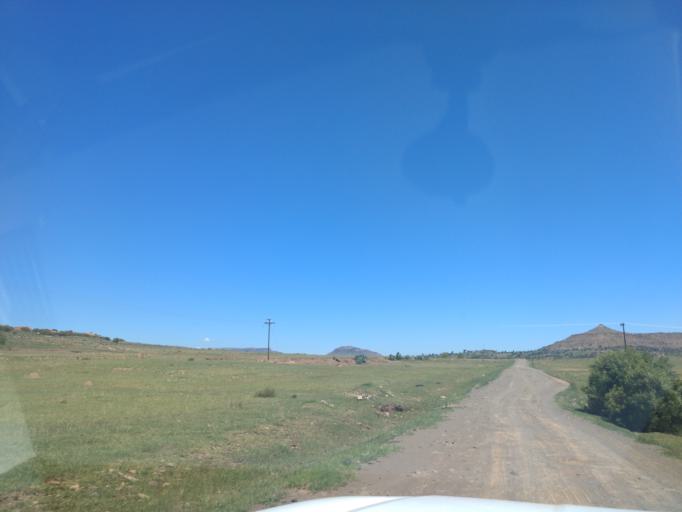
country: LS
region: Maseru
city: Maseru
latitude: -29.4725
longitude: 27.3753
